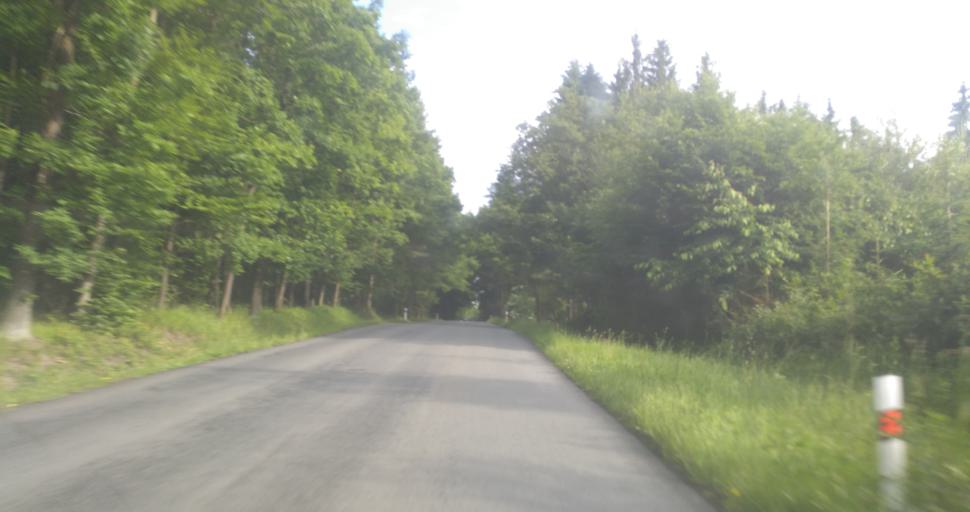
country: CZ
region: Central Bohemia
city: Hudlice
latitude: 49.9632
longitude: 13.9168
